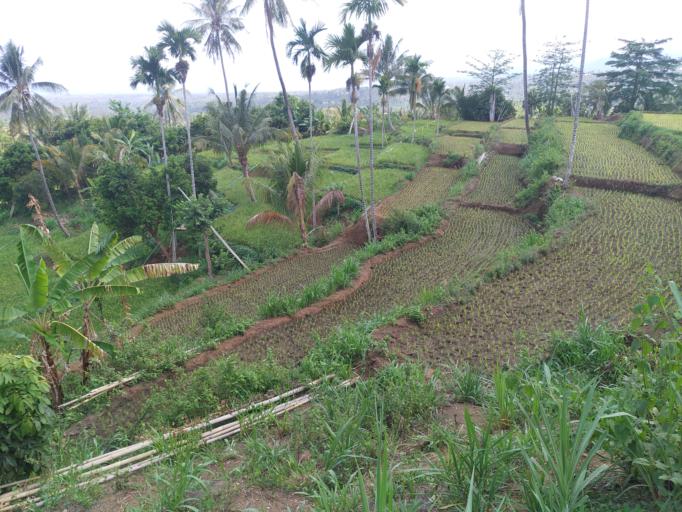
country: ID
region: West Nusa Tenggara
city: Bayan
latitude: -8.2910
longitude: 116.4033
